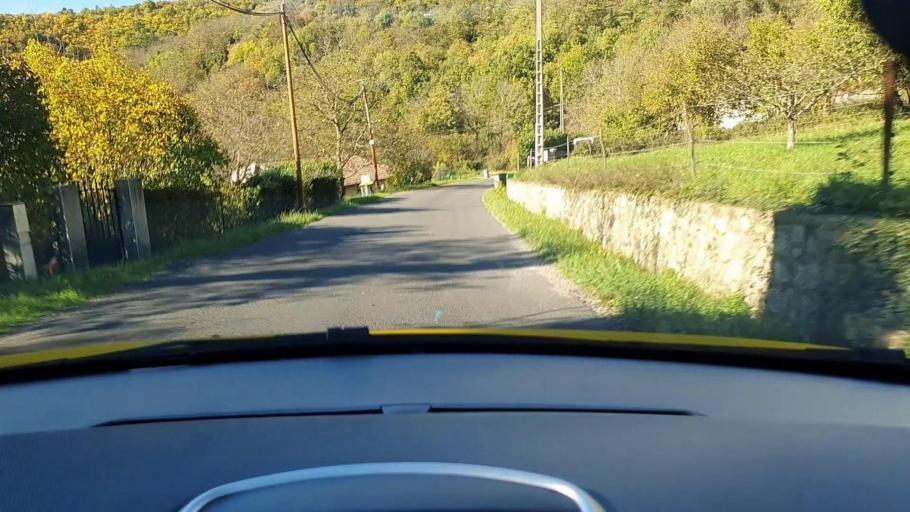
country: FR
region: Languedoc-Roussillon
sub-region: Departement du Gard
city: Le Vigan
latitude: 43.9874
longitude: 3.4992
